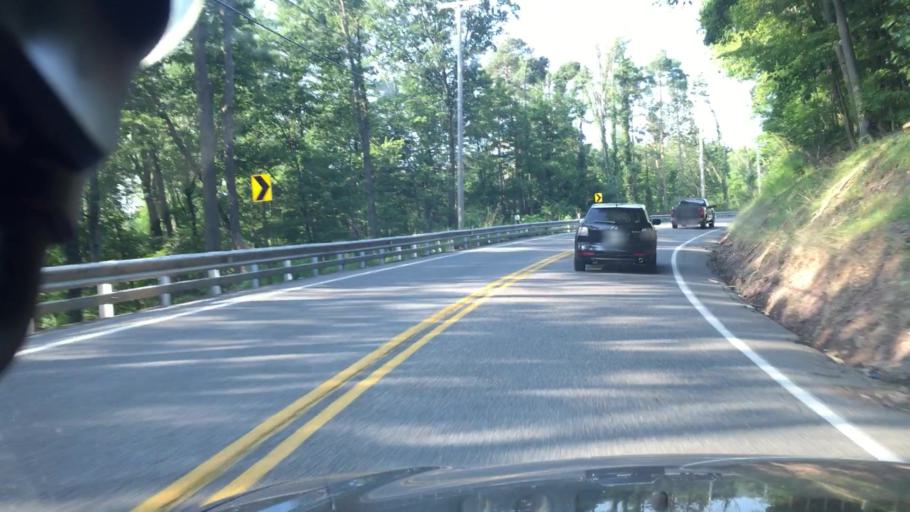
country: US
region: Pennsylvania
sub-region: Columbia County
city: Catawissa
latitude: 40.9173
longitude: -76.4739
